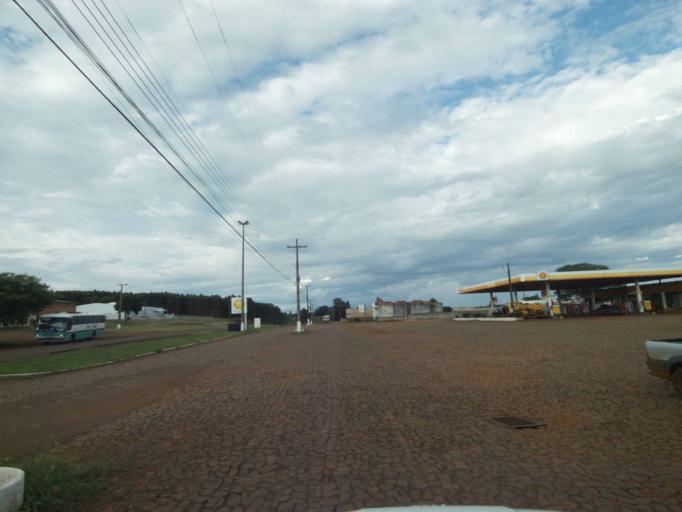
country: BR
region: Parana
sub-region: Laranjeiras Do Sul
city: Laranjeiras do Sul
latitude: -25.4855
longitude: -52.5222
